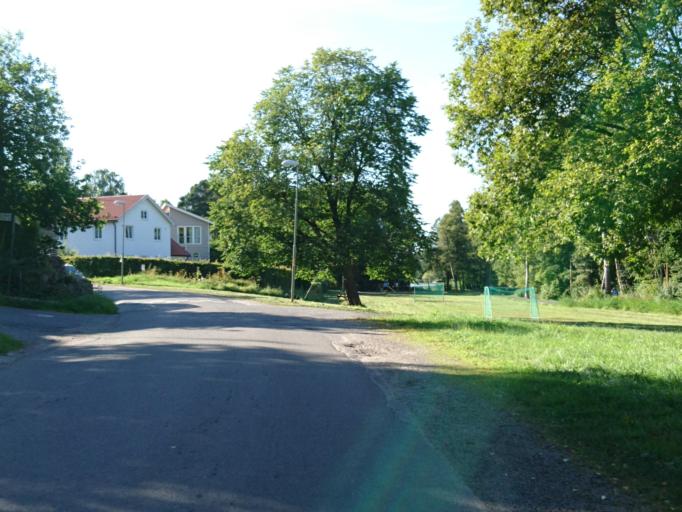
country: SE
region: Stockholm
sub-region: Huddinge Kommun
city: Huddinge
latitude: 59.2616
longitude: 17.9838
